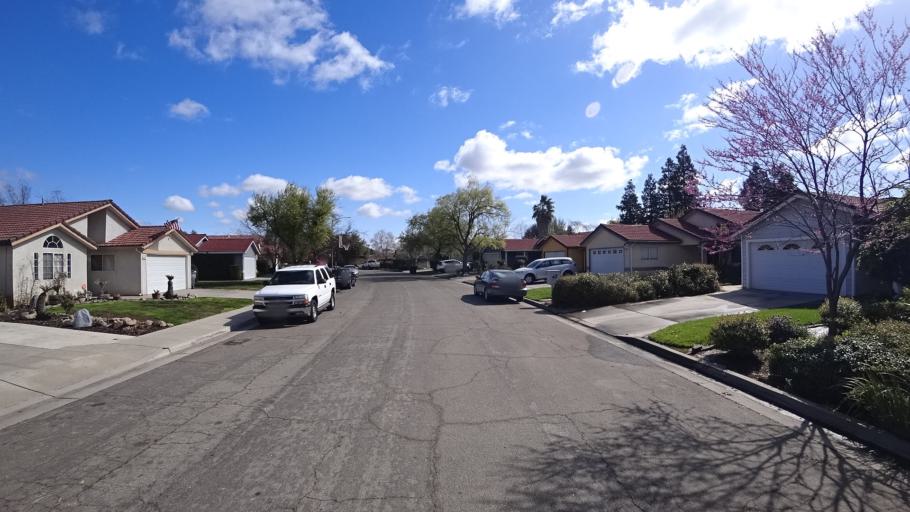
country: US
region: California
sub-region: Fresno County
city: West Park
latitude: 36.8348
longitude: -119.8845
